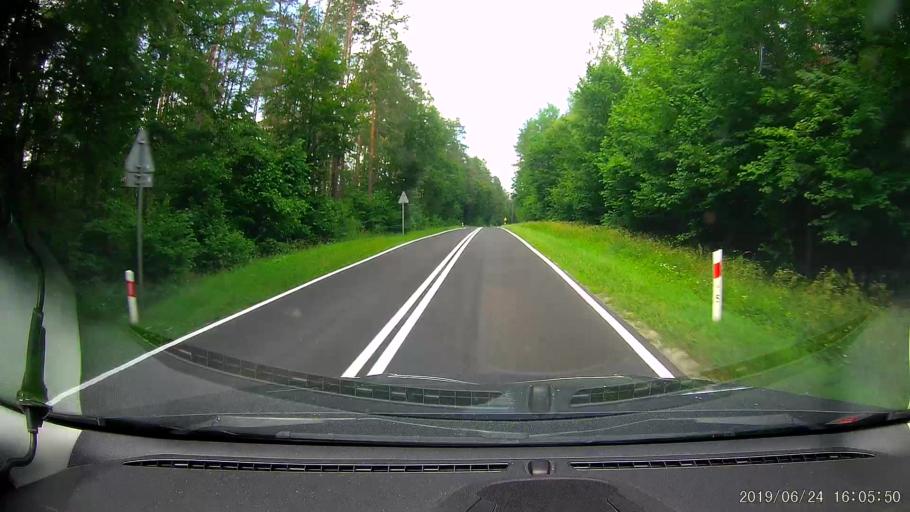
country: PL
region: Subcarpathian Voivodeship
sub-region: Powiat lubaczowski
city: Narol
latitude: 50.3345
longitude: 23.2934
